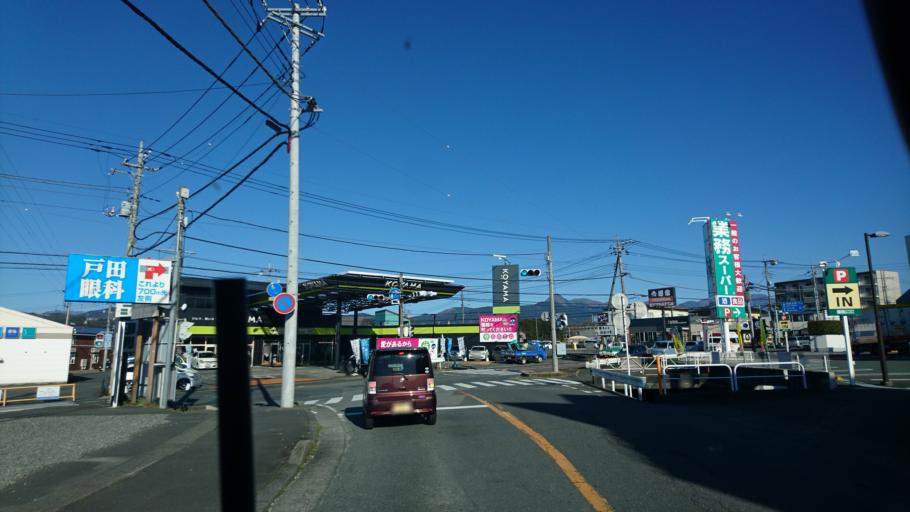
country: JP
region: Shizuoka
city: Fujinomiya
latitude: 35.2416
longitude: 138.6103
